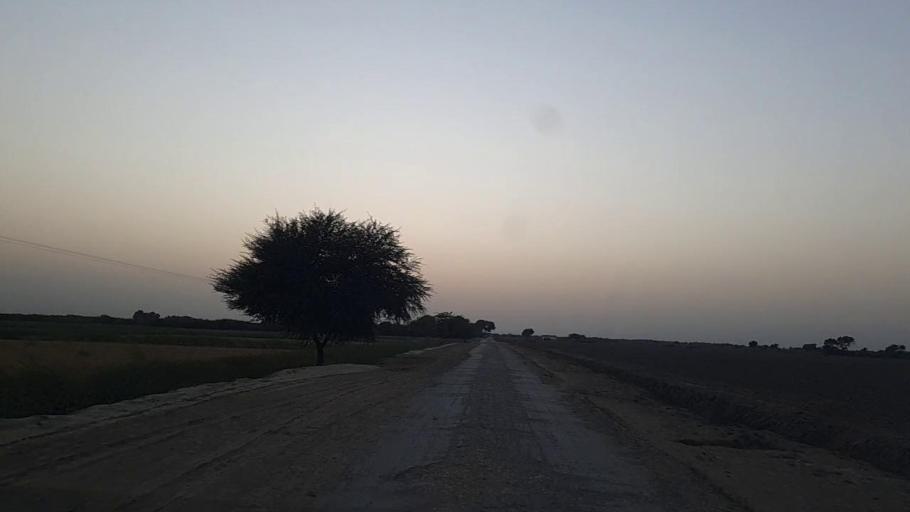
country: PK
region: Sindh
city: Naukot
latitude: 24.7531
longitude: 69.2926
